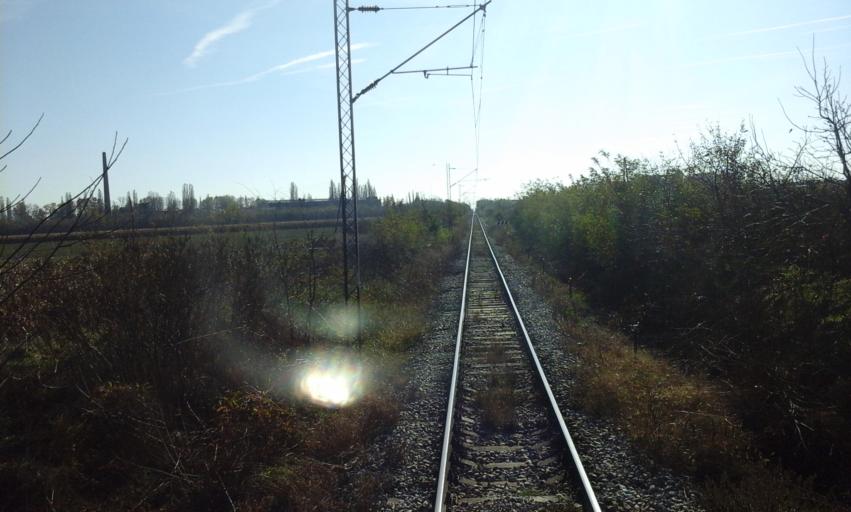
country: RS
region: Autonomna Pokrajina Vojvodina
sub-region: Severnobacki Okrug
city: Subotica
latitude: 46.0743
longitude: 19.6890
